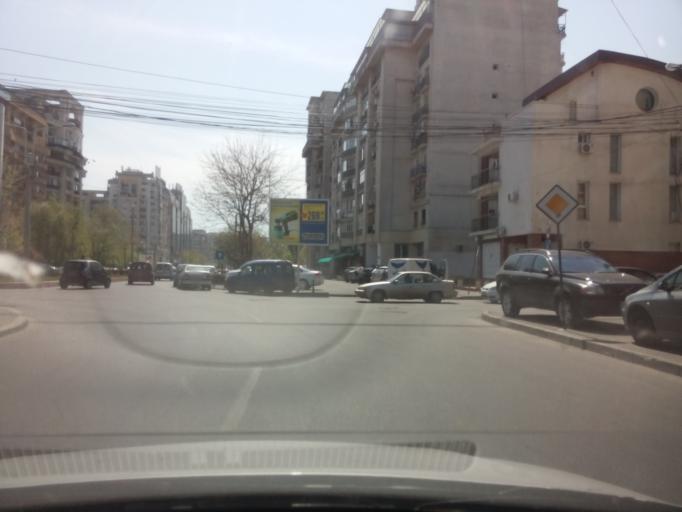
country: RO
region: Bucuresti
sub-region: Municipiul Bucuresti
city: Bucharest
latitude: 44.4279
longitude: 26.1190
